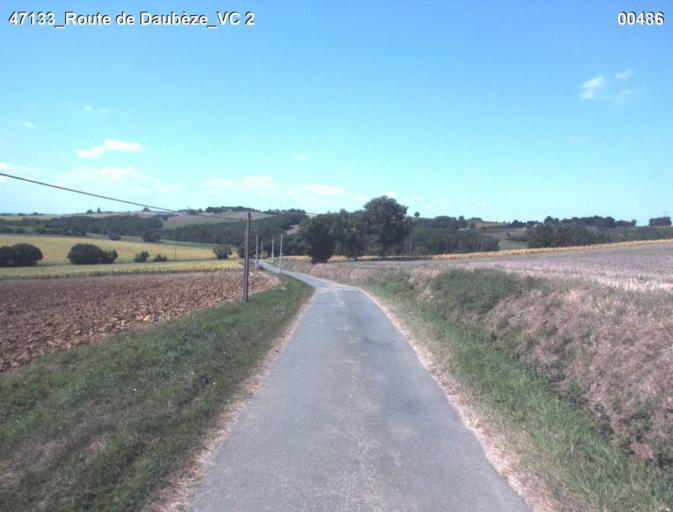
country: FR
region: Aquitaine
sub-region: Departement du Lot-et-Garonne
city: Laplume
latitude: 44.0835
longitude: 0.5391
